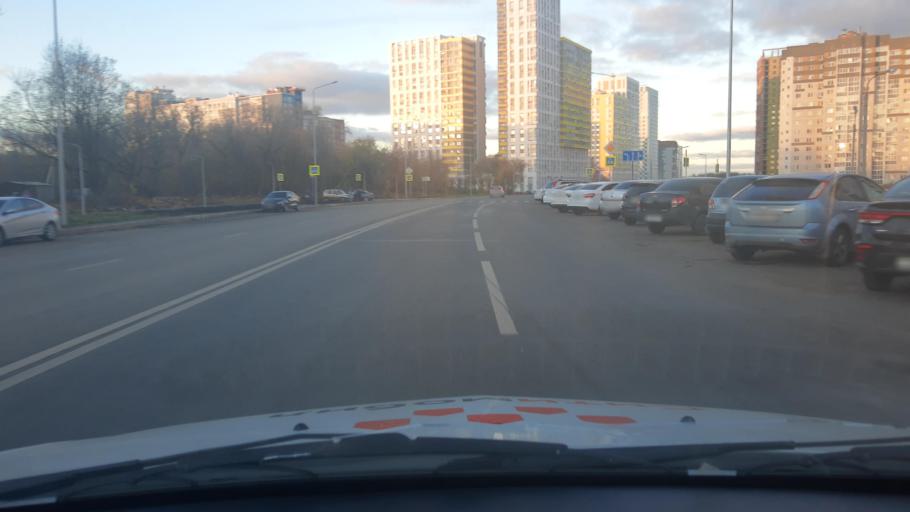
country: RU
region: Bashkortostan
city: Ufa
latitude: 54.7602
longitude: 56.0301
